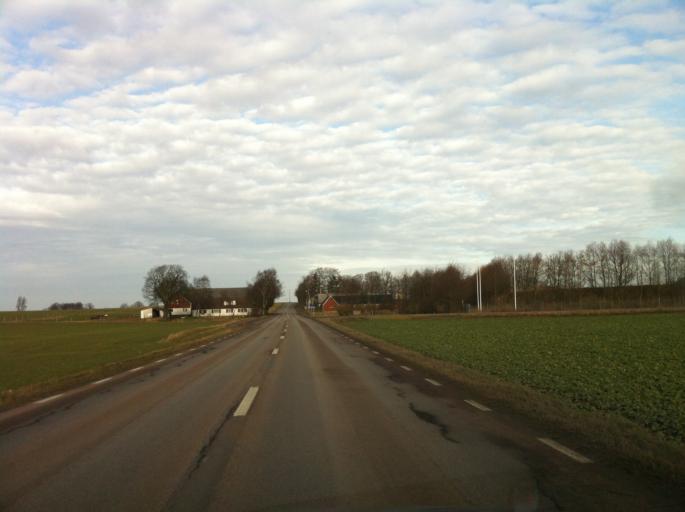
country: SE
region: Skane
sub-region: Landskrona
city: Asmundtorp
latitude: 55.9468
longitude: 12.9483
